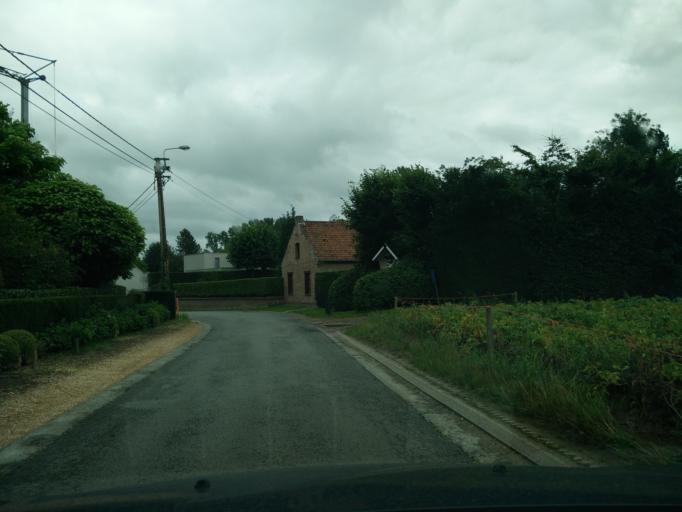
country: BE
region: Flanders
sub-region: Provincie Oost-Vlaanderen
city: Merelbeke
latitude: 50.9509
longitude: 3.7313
